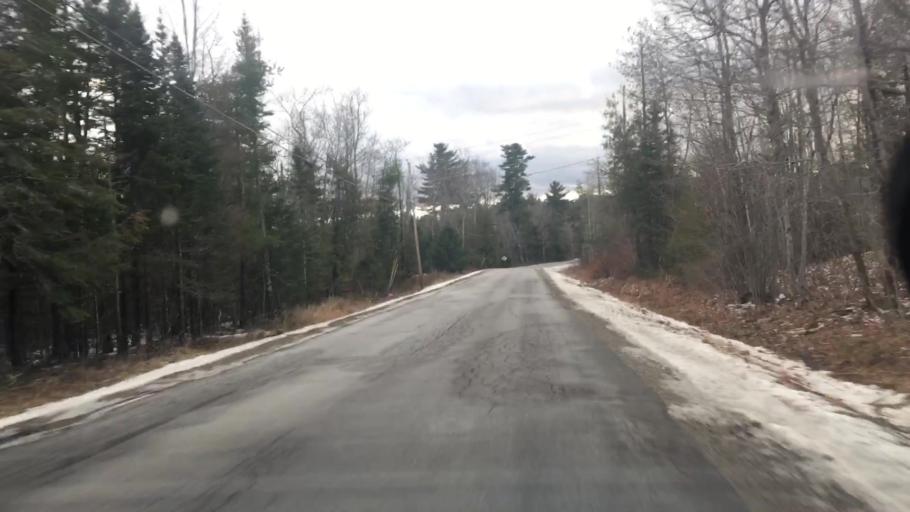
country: US
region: Maine
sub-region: Hancock County
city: Dedham
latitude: 44.6511
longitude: -68.7037
